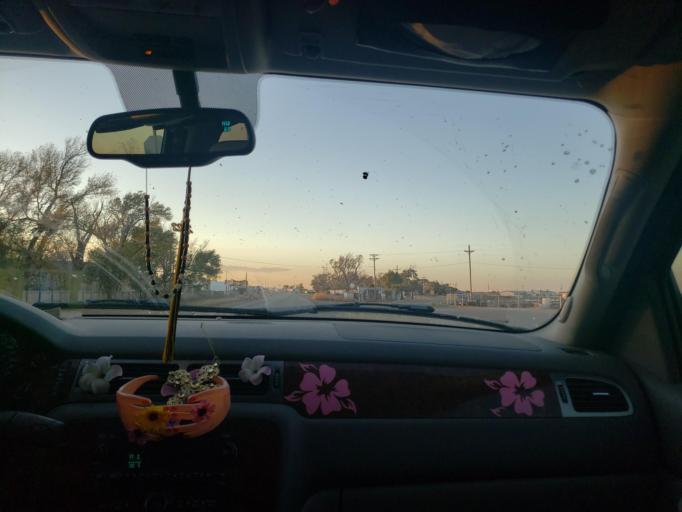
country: US
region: Kansas
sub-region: Finney County
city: Garden City
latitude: 37.9851
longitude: -100.9088
